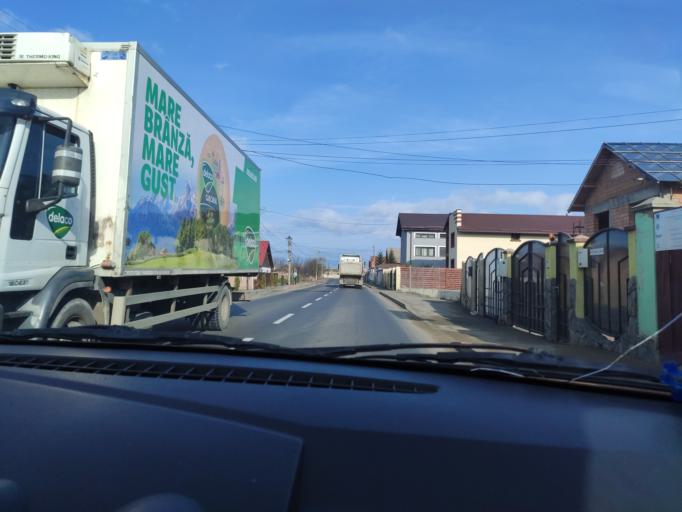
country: RO
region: Brasov
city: Codlea
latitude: 45.7022
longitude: 25.4564
